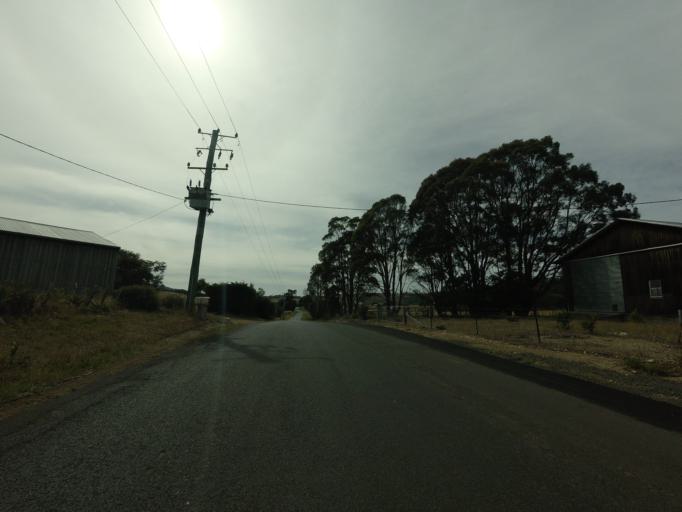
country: AU
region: Tasmania
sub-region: Sorell
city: Sorell
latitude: -42.4262
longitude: 147.5087
